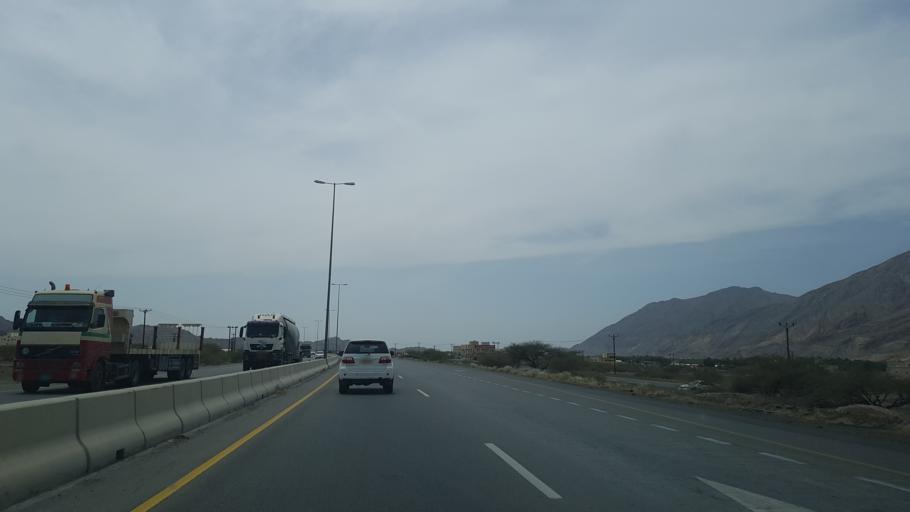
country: OM
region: Muhafazat ad Dakhiliyah
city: Izki
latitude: 23.0137
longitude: 57.7920
